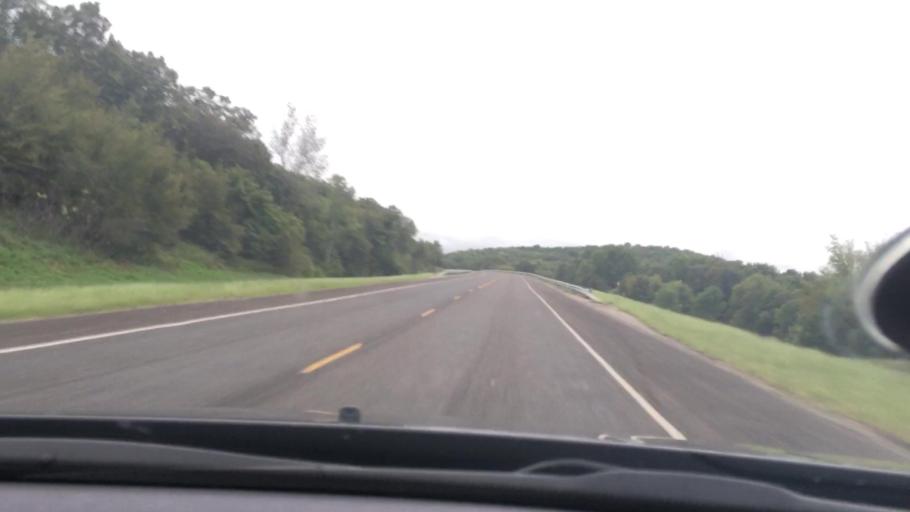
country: US
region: Oklahoma
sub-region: Sequoyah County
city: Vian
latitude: 35.5307
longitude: -94.9731
